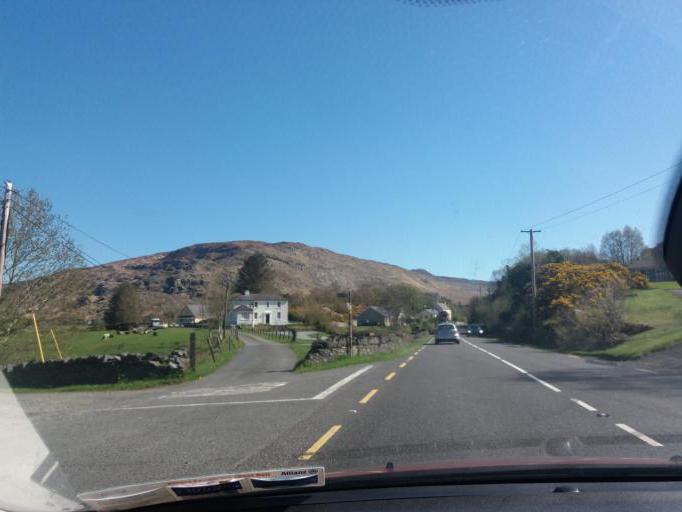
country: IE
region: Munster
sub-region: Ciarrai
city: Cill Airne
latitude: 51.9761
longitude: -9.3348
